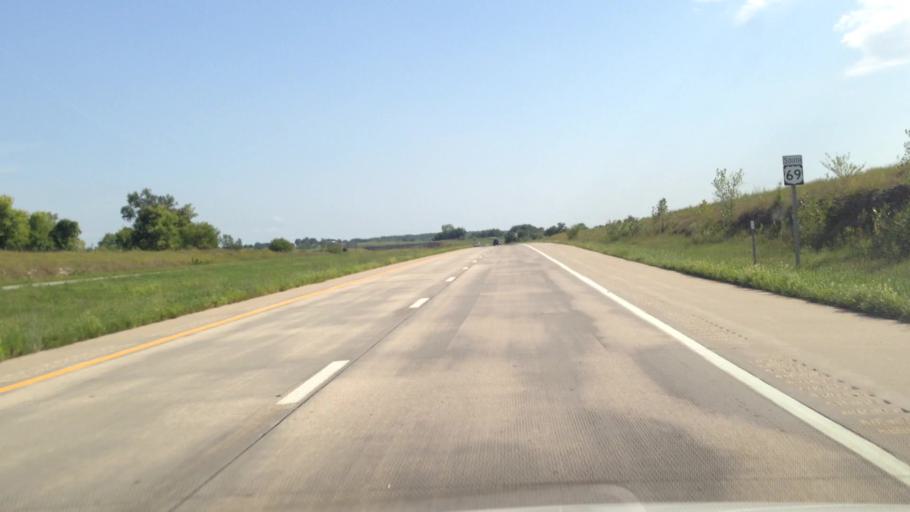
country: US
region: Kansas
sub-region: Miami County
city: Louisburg
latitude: 38.5566
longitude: -94.6916
